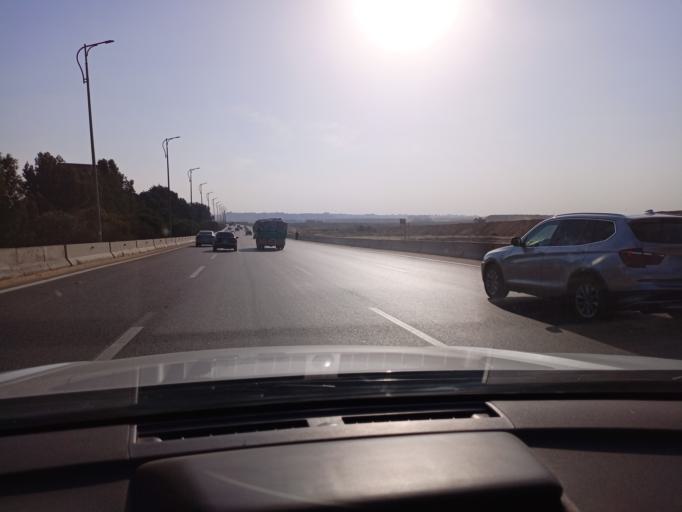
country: EG
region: Muhafazat al Qalyubiyah
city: Al Khankah
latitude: 30.0688
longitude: 31.4251
